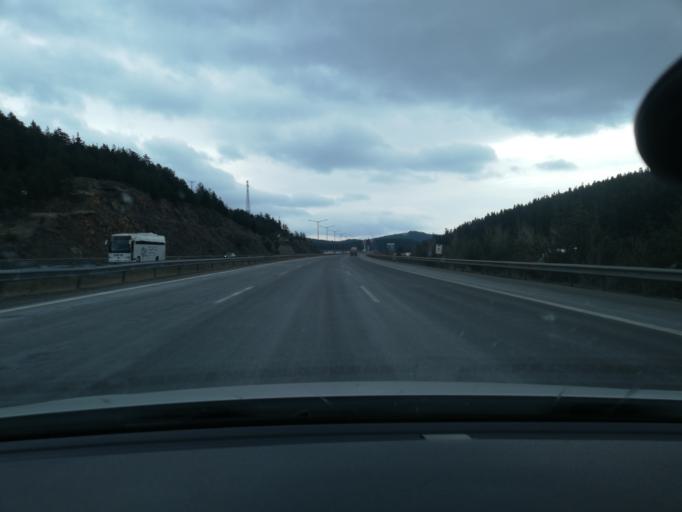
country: TR
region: Bolu
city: Gerede
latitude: 40.6179
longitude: 32.2455
